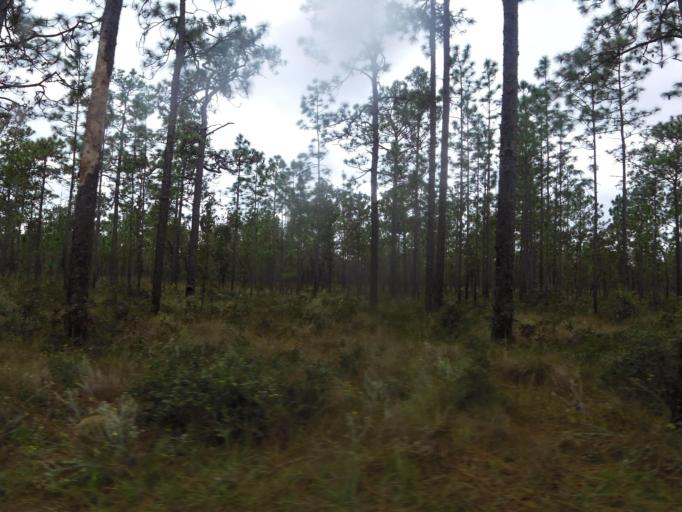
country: US
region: Florida
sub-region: Clay County
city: Keystone Heights
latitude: 29.8459
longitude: -81.9547
